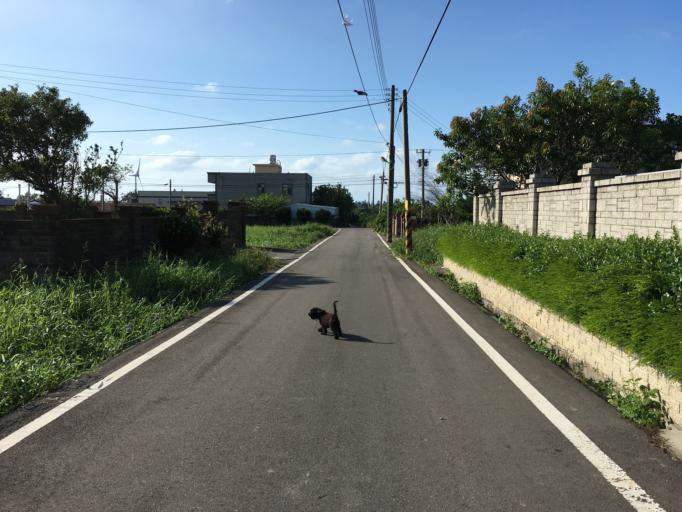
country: TW
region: Taiwan
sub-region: Hsinchu
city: Zhubei
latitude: 24.9233
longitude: 120.9840
